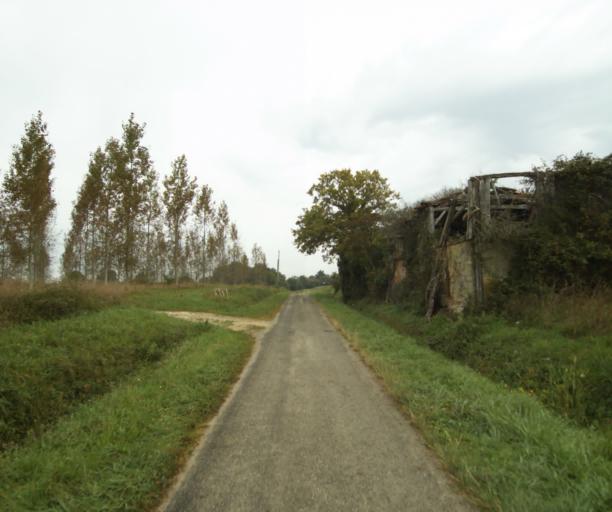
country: FR
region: Midi-Pyrenees
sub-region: Departement du Gers
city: Cazaubon
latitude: 43.9299
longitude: -0.1430
